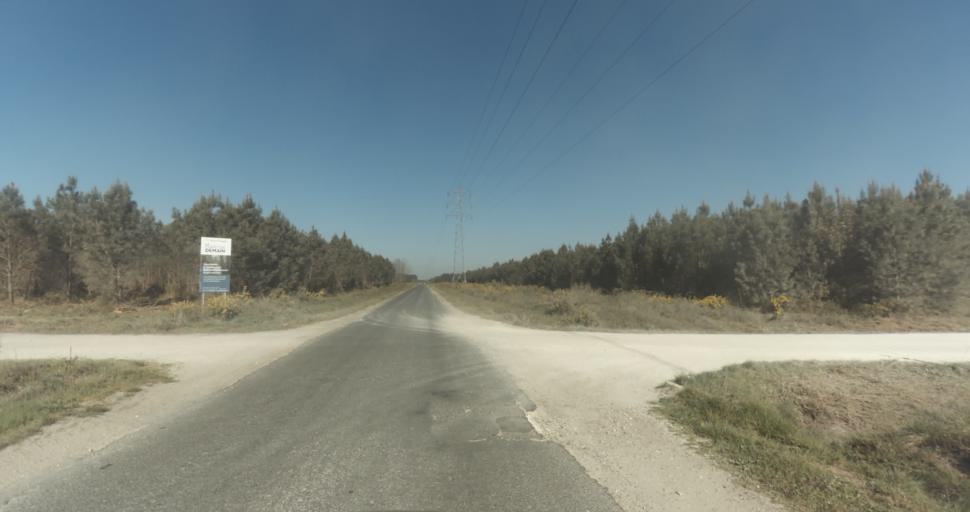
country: FR
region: Aquitaine
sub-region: Departement de la Gironde
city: Marcheprime
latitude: 44.7489
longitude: -0.8435
